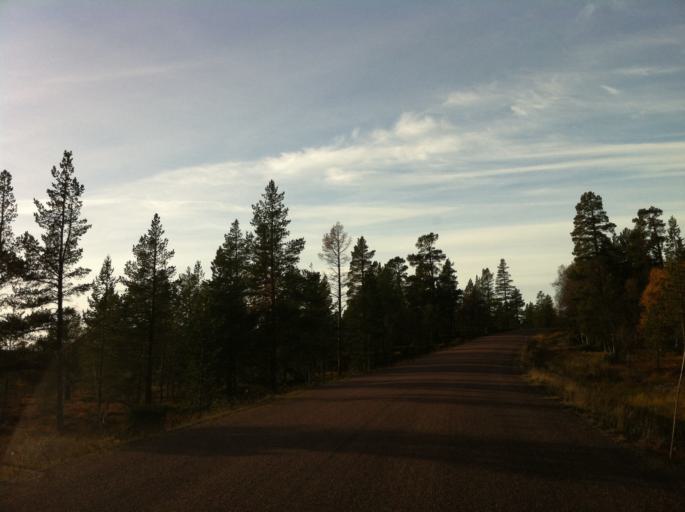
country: NO
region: Hedmark
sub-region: Engerdal
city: Engerdal
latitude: 62.0829
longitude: 12.1254
